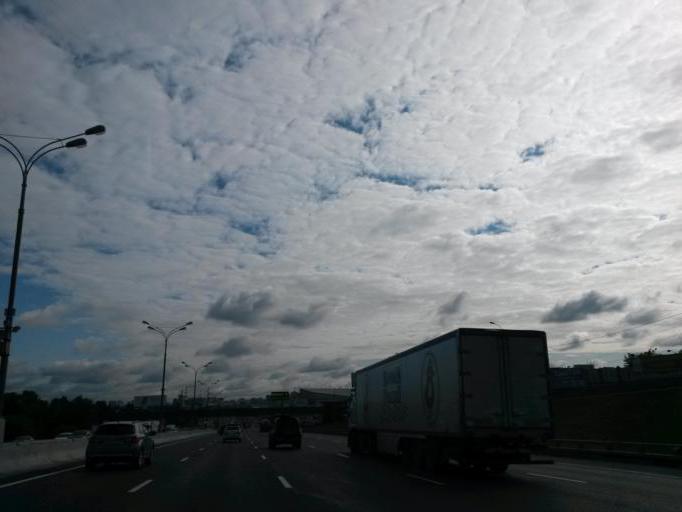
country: RU
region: Moskovskaya
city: Kotel'niki
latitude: 55.6421
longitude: 37.8223
